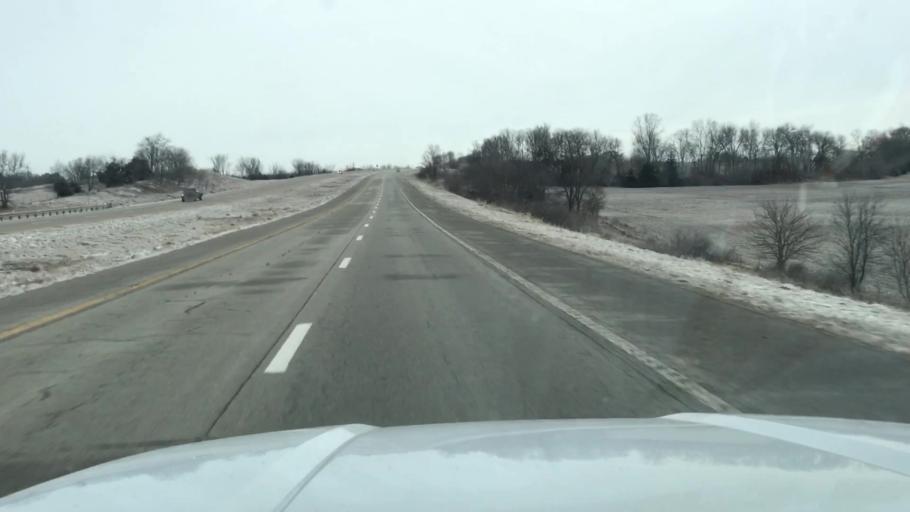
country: US
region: Missouri
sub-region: Andrew County
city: Savannah
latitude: 39.9074
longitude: -94.8588
